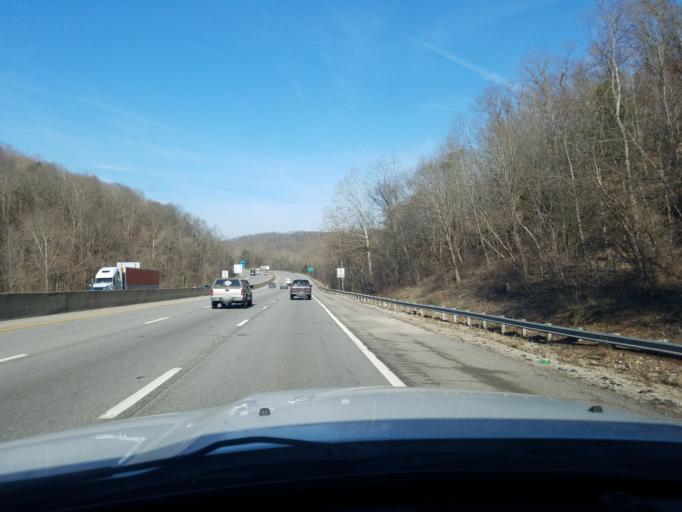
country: US
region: West Virginia
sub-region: Kanawha County
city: Cross Lanes
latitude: 38.4243
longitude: -81.8097
